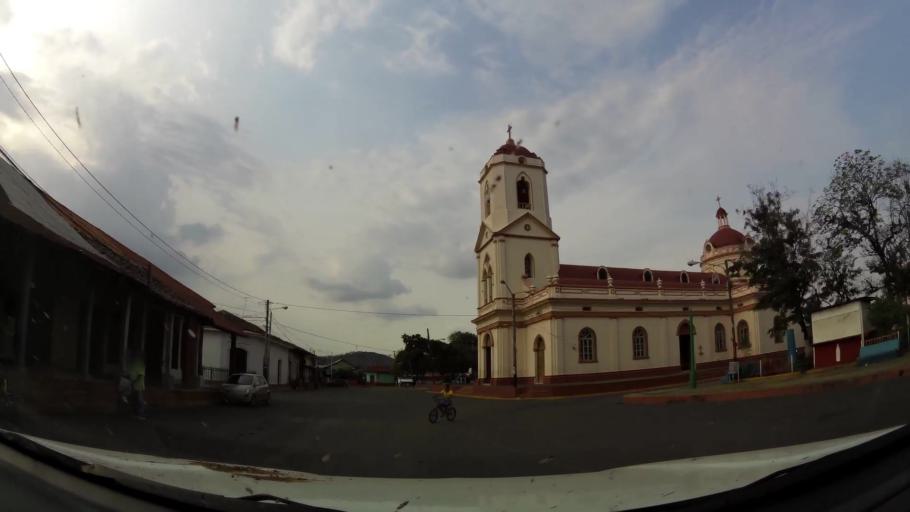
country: NI
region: Masaya
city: Masaya
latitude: 11.9785
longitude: -86.0978
